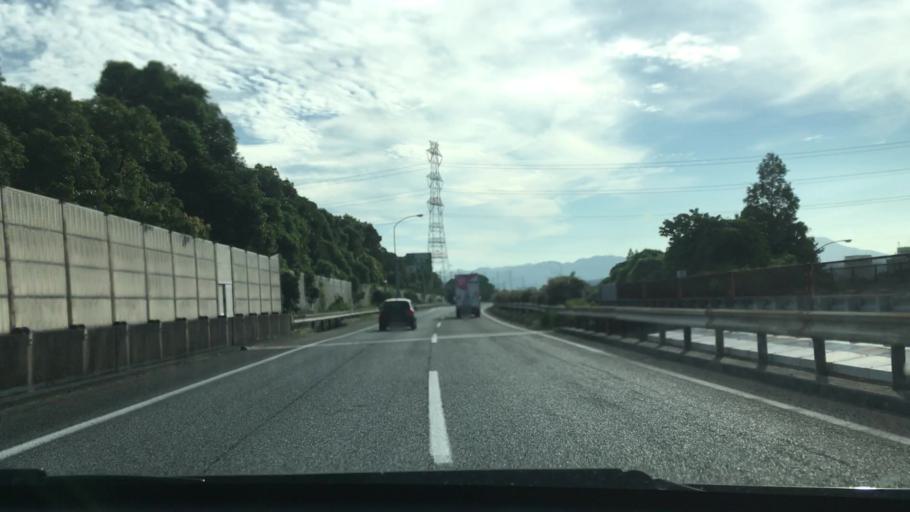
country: JP
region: Fukuoka
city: Kitakyushu
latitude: 33.8337
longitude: 130.9163
